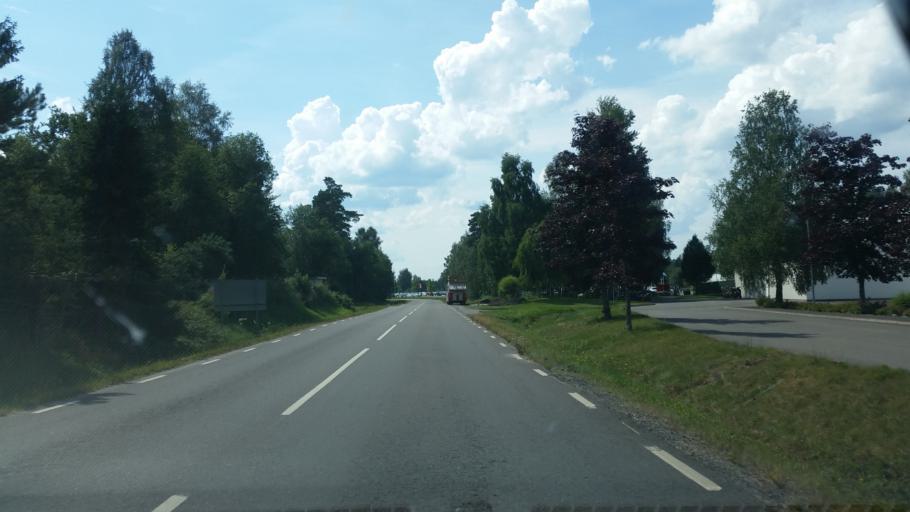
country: SE
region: Vaestra Goetaland
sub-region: Skara Kommun
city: Axvall
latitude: 58.4062
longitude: 13.5544
